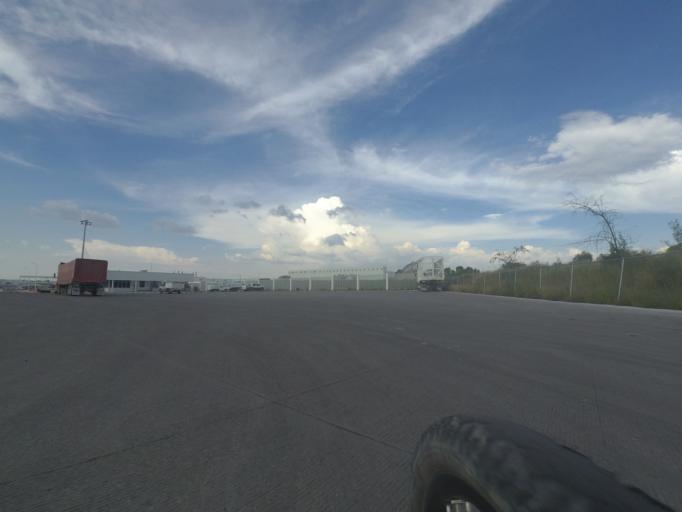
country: MX
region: Aguascalientes
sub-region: Aguascalientes
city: Penuelas (El Cienegal)
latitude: 21.7306
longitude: -102.2822
